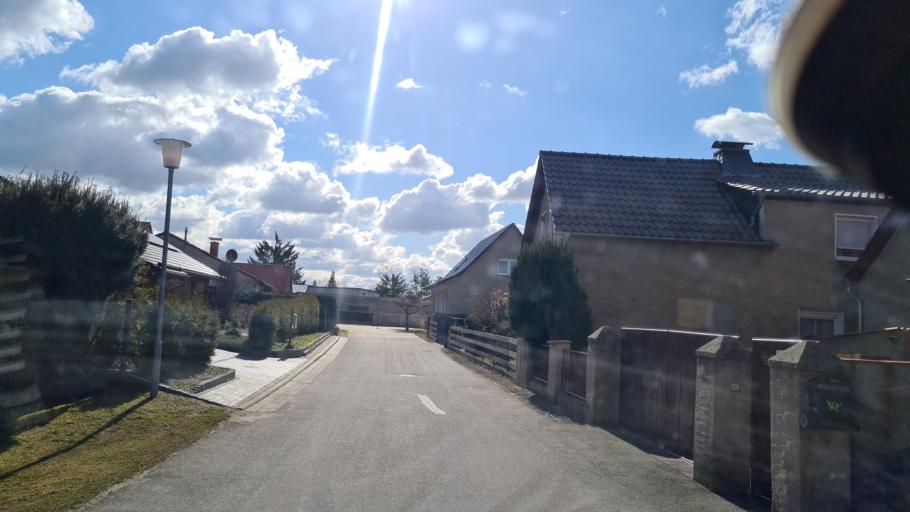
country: DE
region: Brandenburg
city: Falkenberg
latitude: 51.5789
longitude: 13.2090
